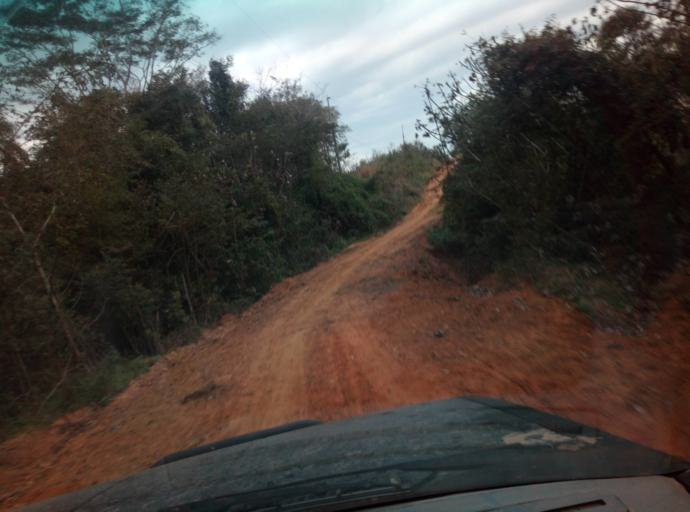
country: PY
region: Caaguazu
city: Doctor Cecilio Baez
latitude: -25.1442
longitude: -56.2243
